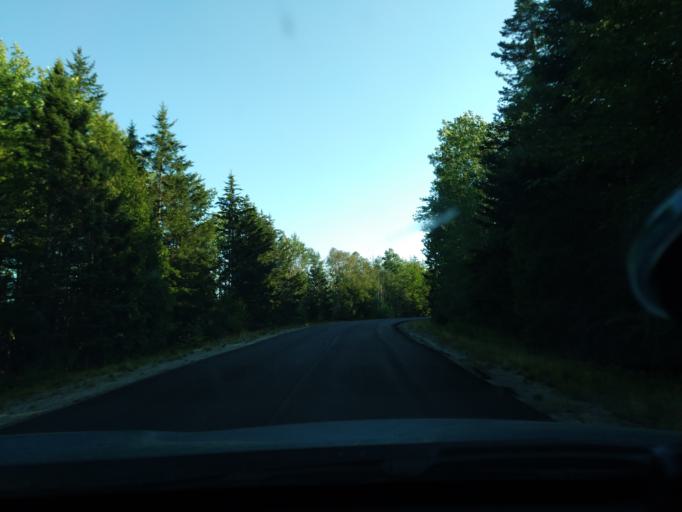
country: US
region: Maine
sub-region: Washington County
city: East Machias
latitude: 44.7093
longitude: -67.1445
